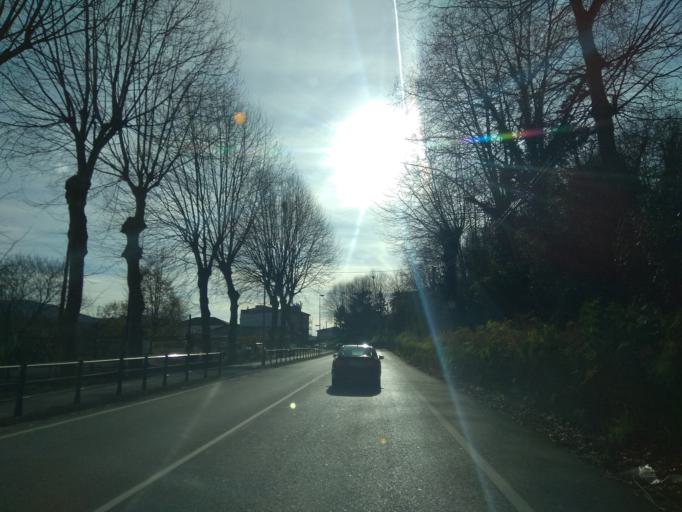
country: ES
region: Cantabria
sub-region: Provincia de Cantabria
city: El Astillero
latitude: 43.4094
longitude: -3.8423
